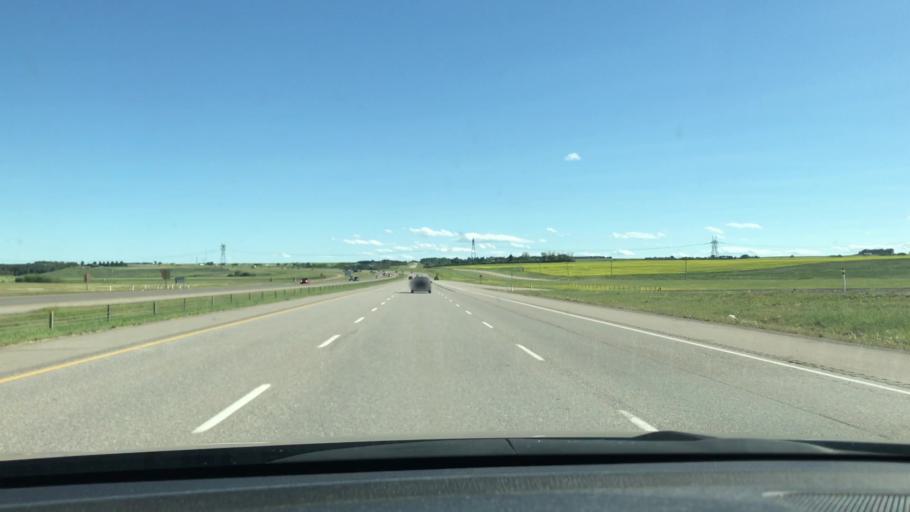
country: CA
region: Alberta
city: Crossfield
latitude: 51.4728
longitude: -114.0253
